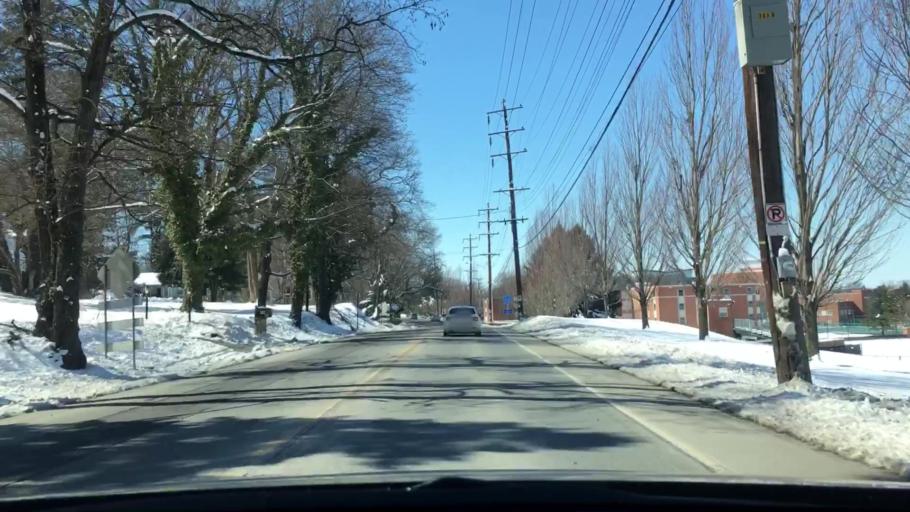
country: US
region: Pennsylvania
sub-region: York County
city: Grantley
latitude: 39.9463
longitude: -76.7240
